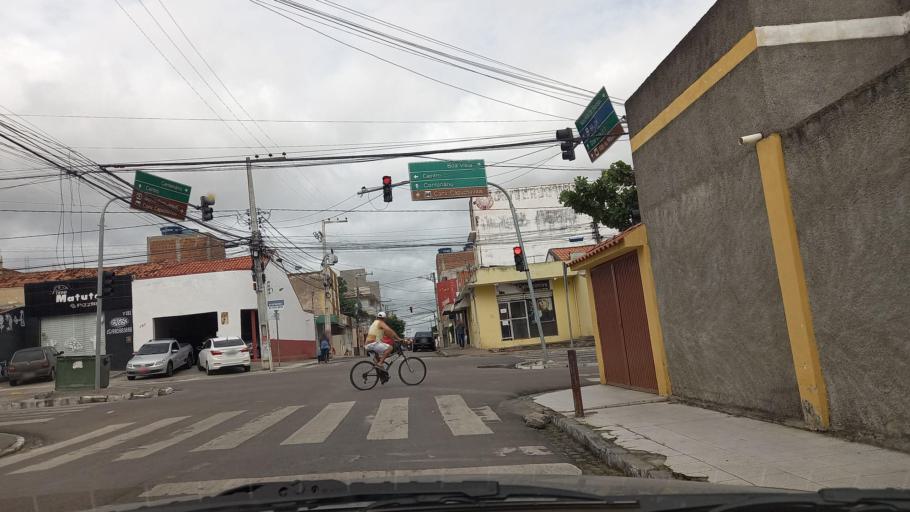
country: BR
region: Pernambuco
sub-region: Caruaru
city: Caruaru
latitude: -8.2792
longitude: -35.9768
